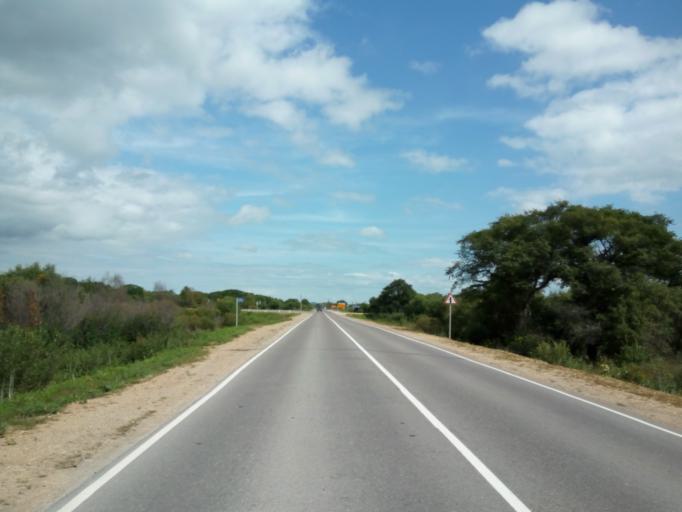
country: RU
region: Primorskiy
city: Dal'nerechensk
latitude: 45.9695
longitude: 133.7852
